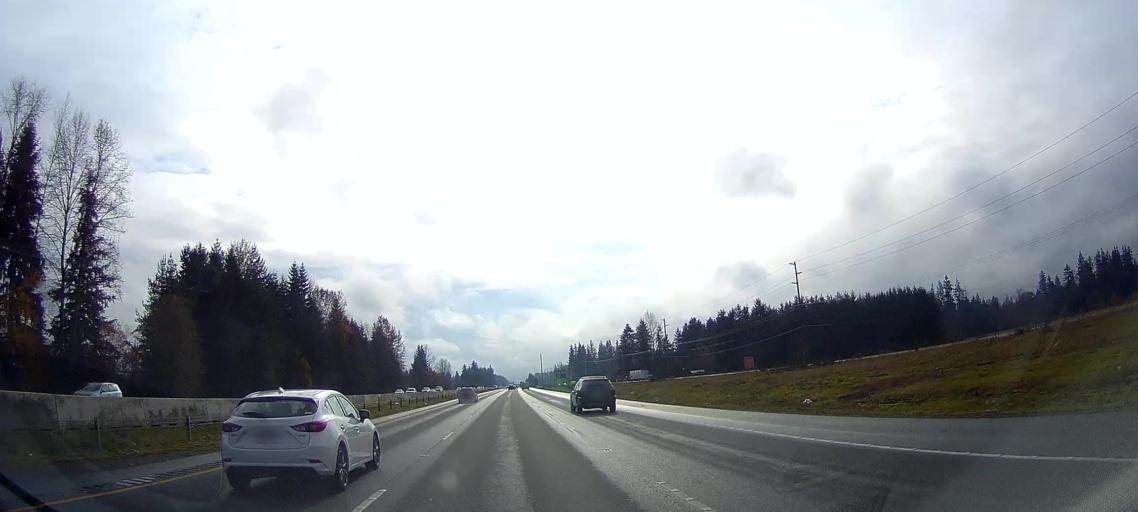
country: US
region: Washington
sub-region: Snohomish County
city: Smokey Point
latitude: 48.1137
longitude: -122.1856
